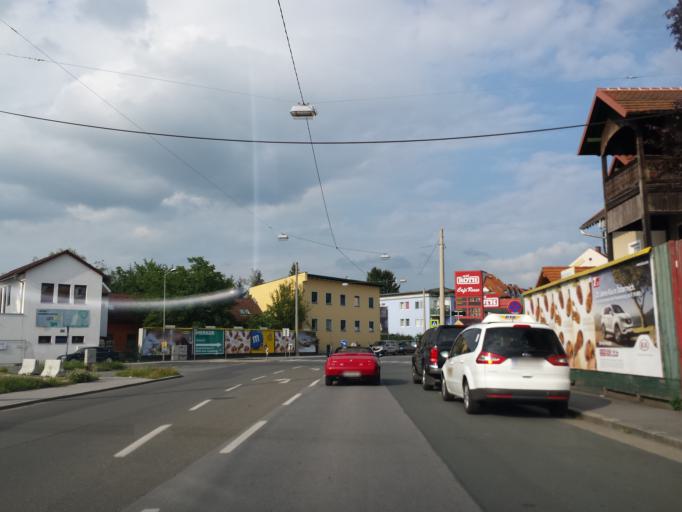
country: AT
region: Styria
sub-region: Graz Stadt
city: Wetzelsdorf
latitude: 47.0626
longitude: 15.3986
